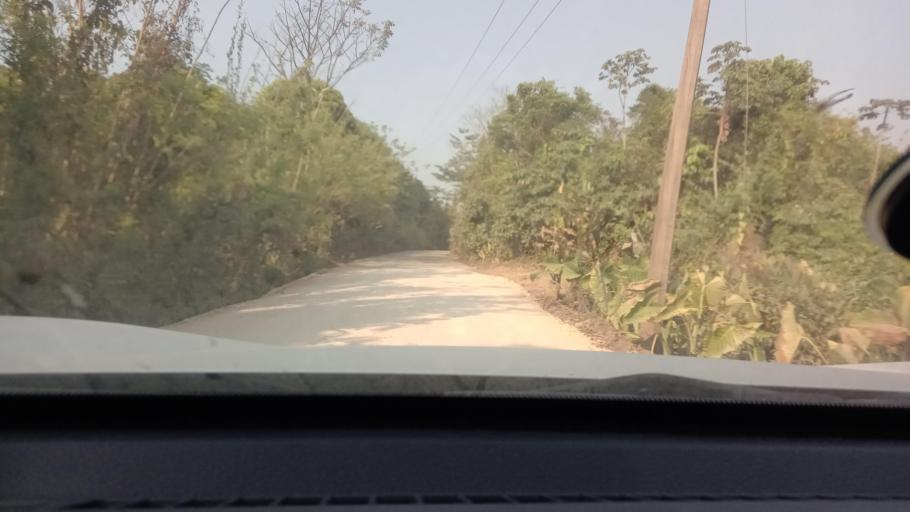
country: MX
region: Tabasco
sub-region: Huimanguillo
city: Francisco Rueda
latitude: 17.6569
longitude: -93.8677
